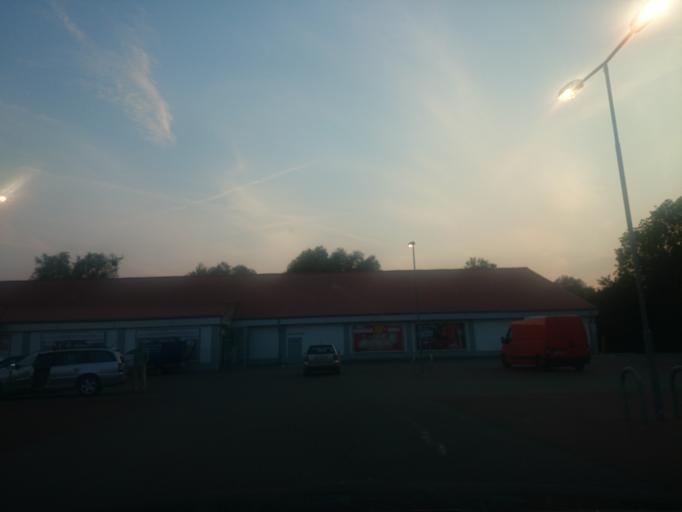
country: PL
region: West Pomeranian Voivodeship
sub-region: Szczecin
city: Szczecin
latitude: 53.4087
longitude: 14.5101
